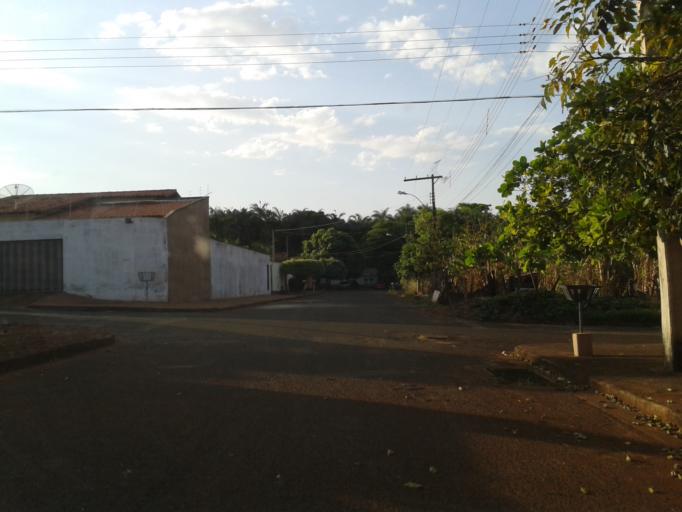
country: BR
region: Minas Gerais
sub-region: Ituiutaba
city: Ituiutaba
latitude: -18.9853
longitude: -49.4433
